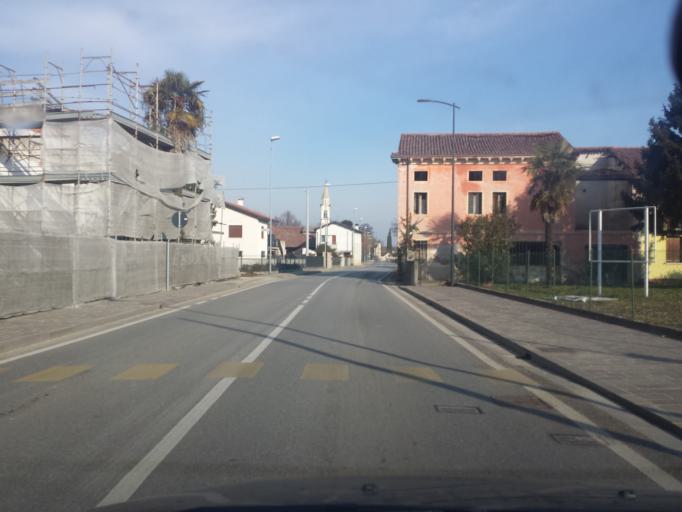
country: IT
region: Veneto
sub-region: Provincia di Vicenza
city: Bressanvido
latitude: 45.6461
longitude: 11.6333
